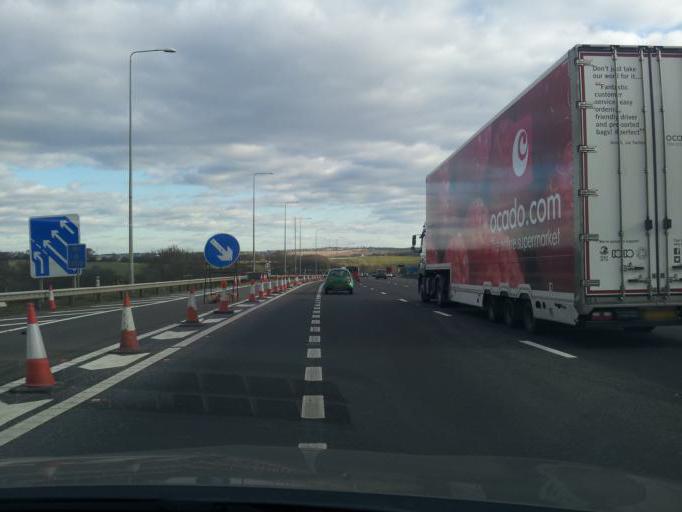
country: GB
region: England
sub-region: Derbyshire
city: Pinxton
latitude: 53.0981
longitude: -1.3168
